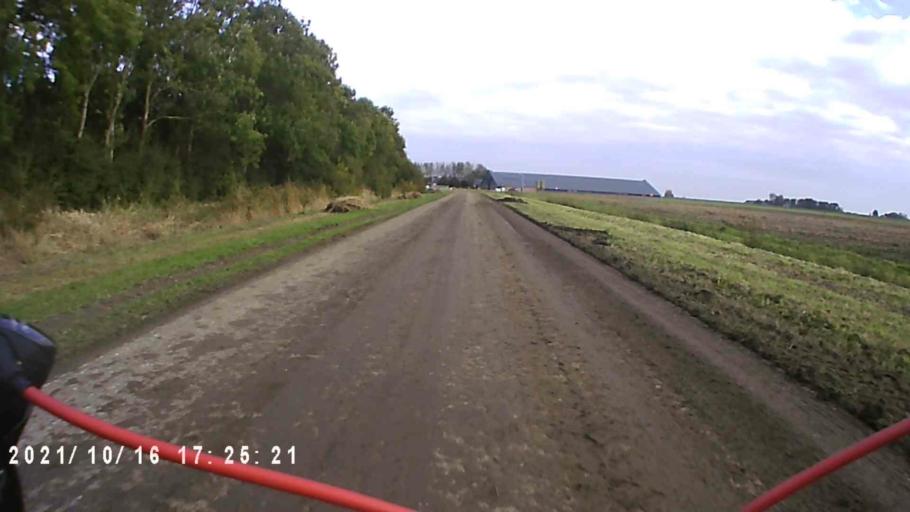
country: NL
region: Friesland
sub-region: Gemeente Kollumerland en Nieuwkruisland
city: Kollum
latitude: 53.3210
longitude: 6.1886
